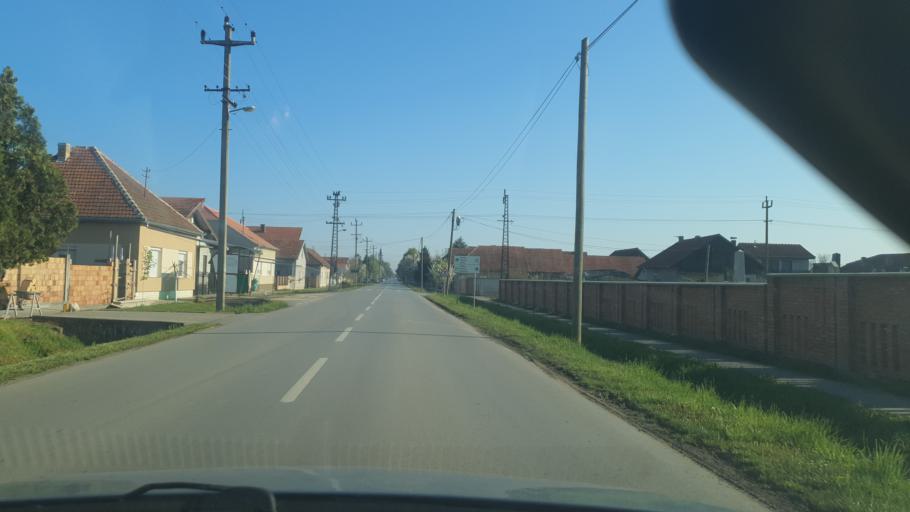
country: RS
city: Kulpin
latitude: 45.3931
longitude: 19.5875
